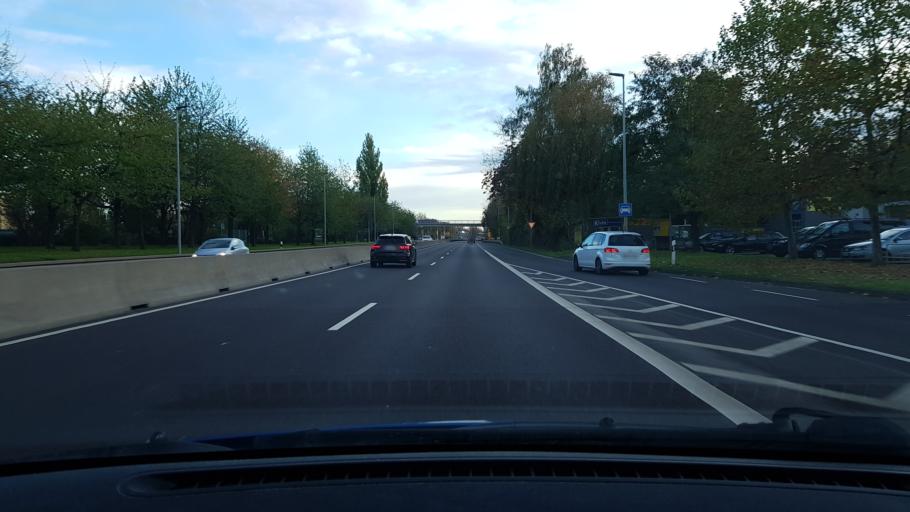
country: DE
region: Saxony-Anhalt
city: Neue Neustadt
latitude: 52.1571
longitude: 11.6274
